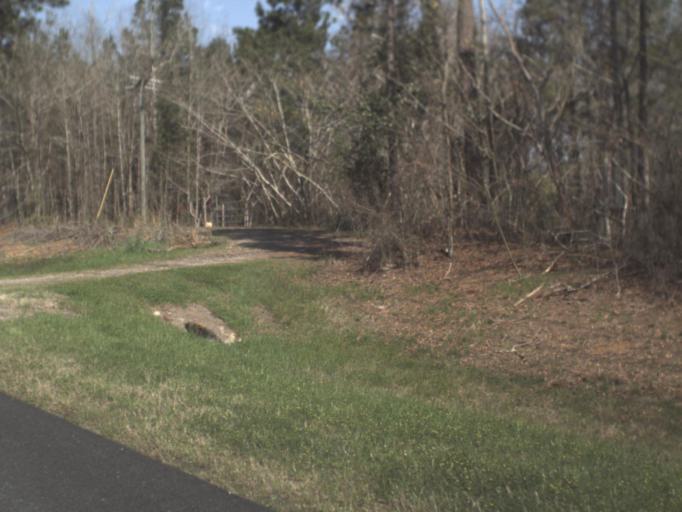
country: US
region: Florida
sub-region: Gadsden County
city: Havana
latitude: 30.5947
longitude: -84.4117
